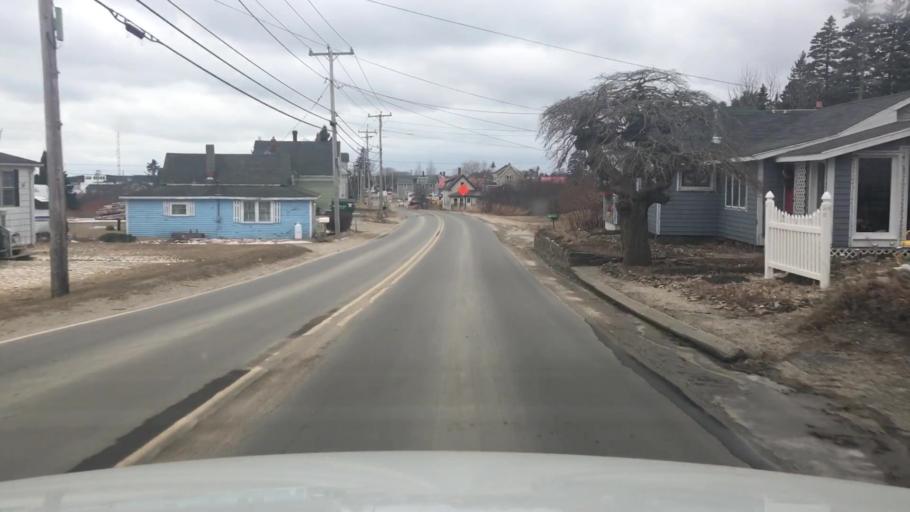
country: US
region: Maine
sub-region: Washington County
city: Jonesport
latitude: 44.5297
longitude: -67.6123
